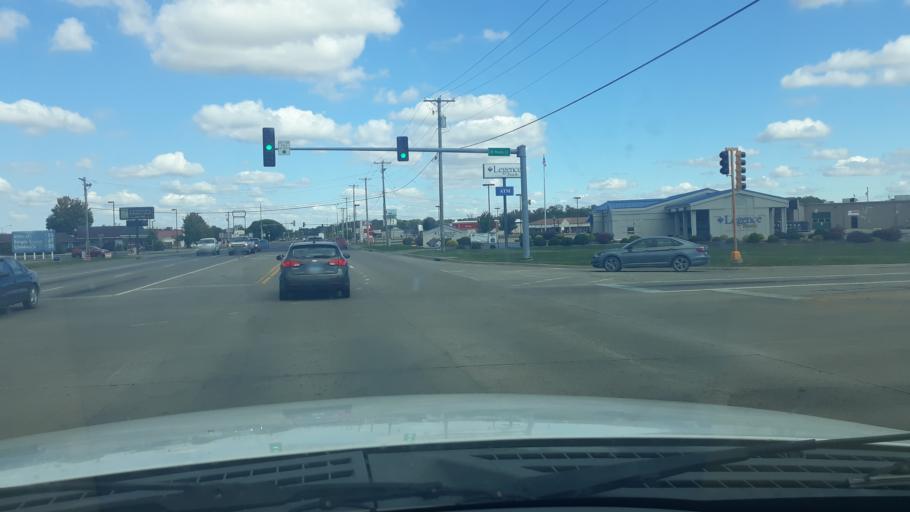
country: US
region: Illinois
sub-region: Saline County
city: Harrisburg
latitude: 37.7414
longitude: -88.5294
